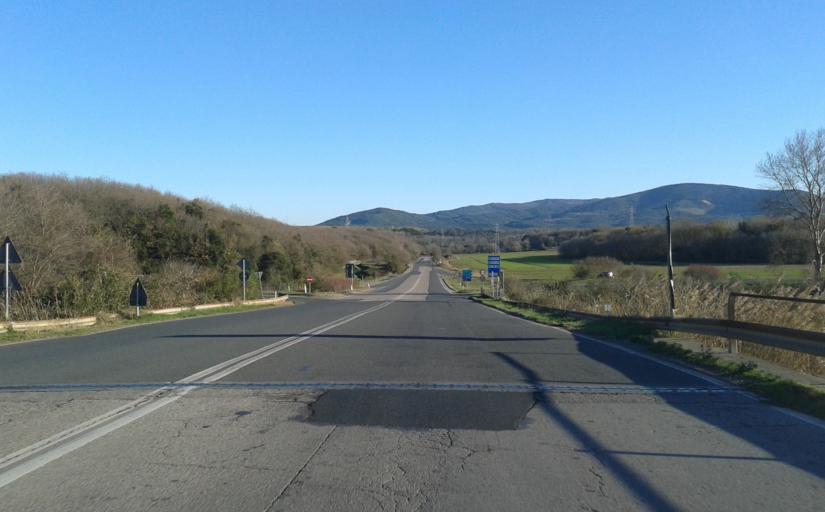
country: IT
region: Tuscany
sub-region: Provincia di Livorno
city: Livorno
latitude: 43.5727
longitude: 10.3498
